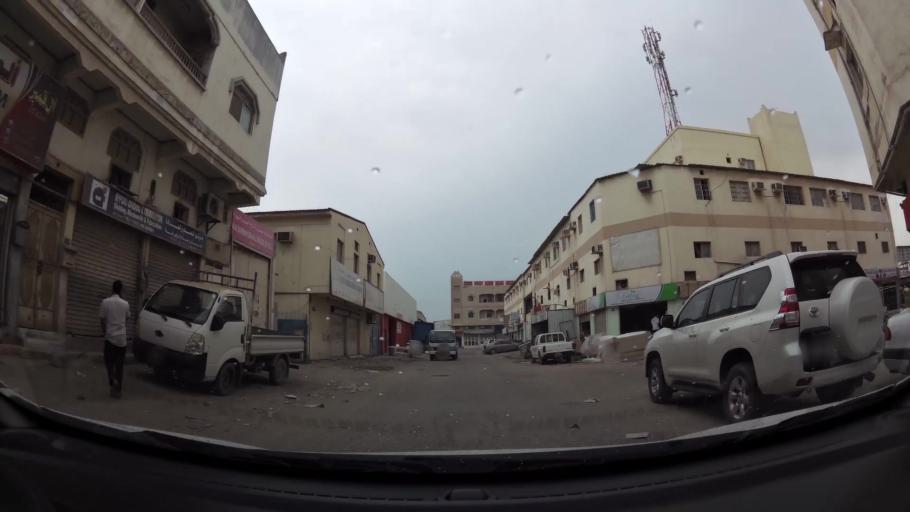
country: BH
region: Northern
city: Madinat `Isa
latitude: 26.1823
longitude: 50.5298
